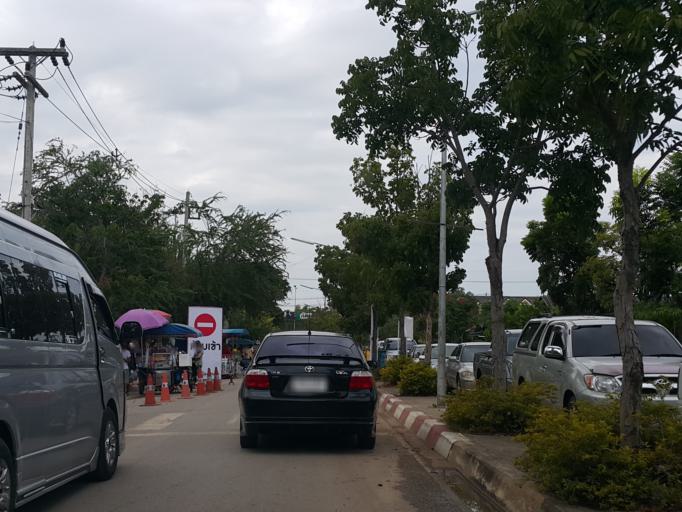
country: TH
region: Lampang
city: Lampang
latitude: 18.2727
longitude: 99.4819
